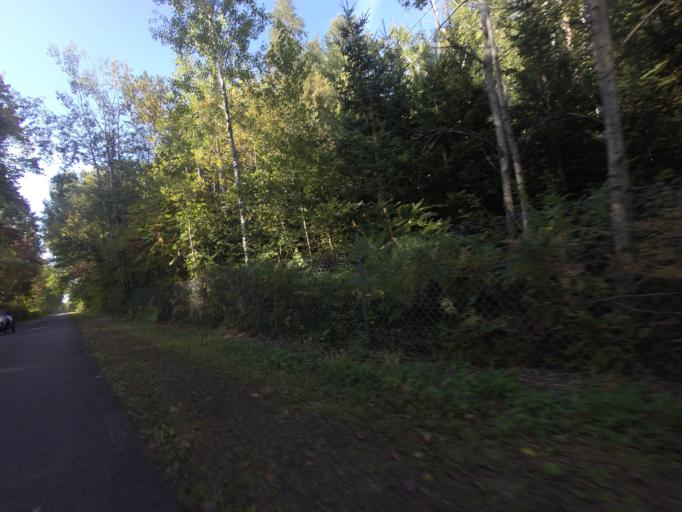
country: CA
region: Quebec
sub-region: Laurentides
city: Saint-Jerome
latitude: 45.7364
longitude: -73.9513
